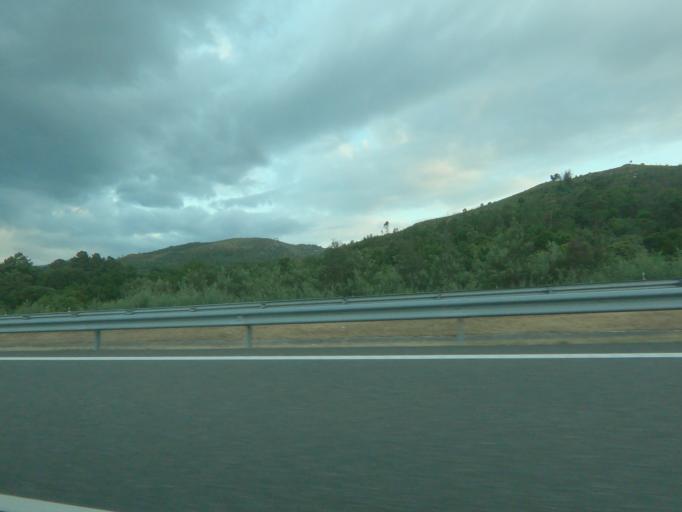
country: ES
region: Galicia
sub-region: Provincia de Ourense
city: Carballeda de Avia
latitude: 42.3101
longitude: -8.1669
